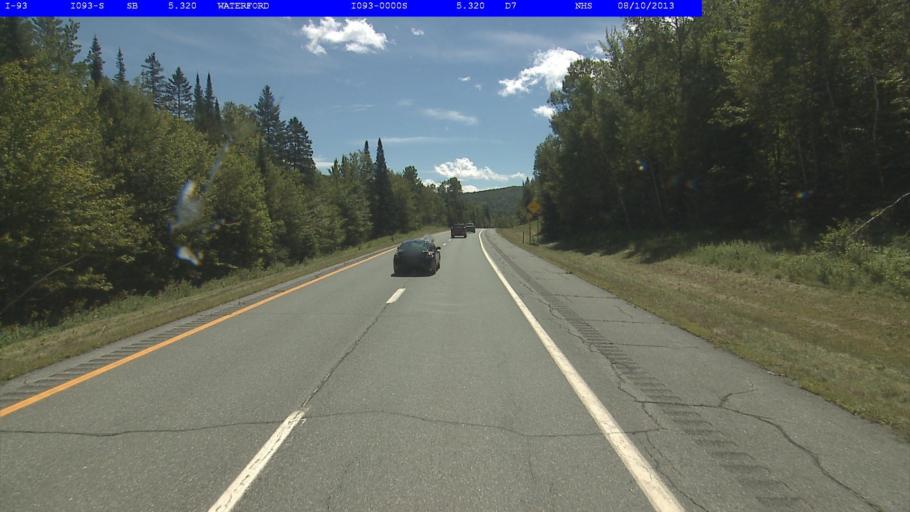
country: US
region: Vermont
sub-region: Caledonia County
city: Saint Johnsbury
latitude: 44.4118
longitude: -71.9225
